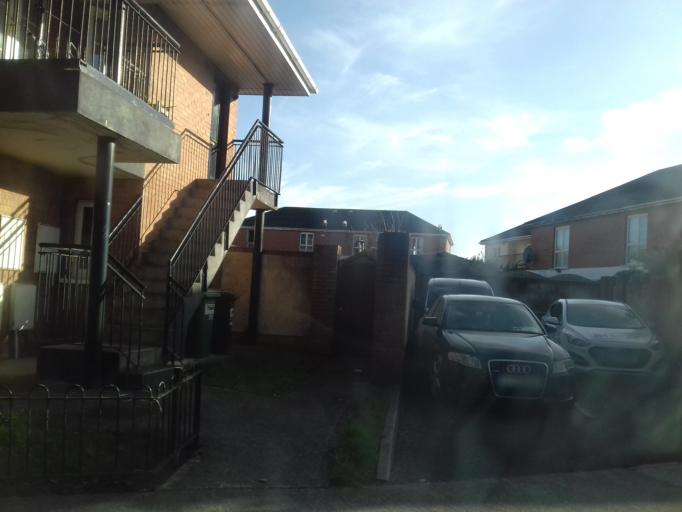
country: IE
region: Leinster
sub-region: Fingal County
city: Blanchardstown
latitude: 53.4166
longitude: -6.3873
